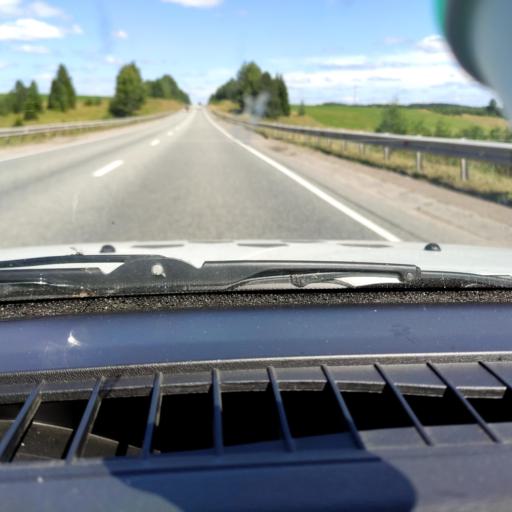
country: RU
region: Udmurtiya
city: Khokhryaki
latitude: 56.9521
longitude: 53.6414
